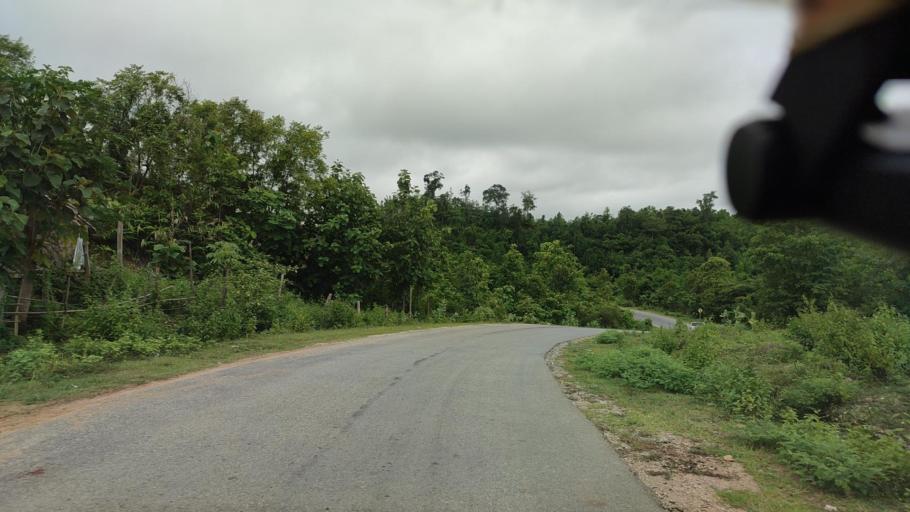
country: MM
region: Magway
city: Taungdwingyi
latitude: 20.0152
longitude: 95.8316
